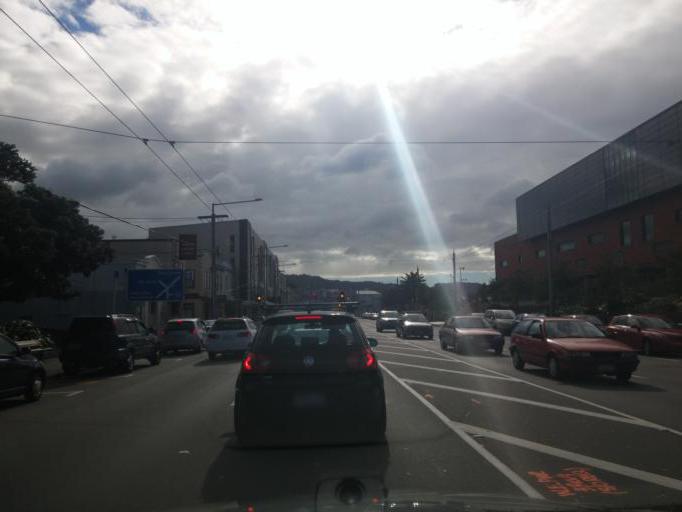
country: NZ
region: Wellington
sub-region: Wellington City
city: Wellington
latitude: -41.3098
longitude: 174.7787
